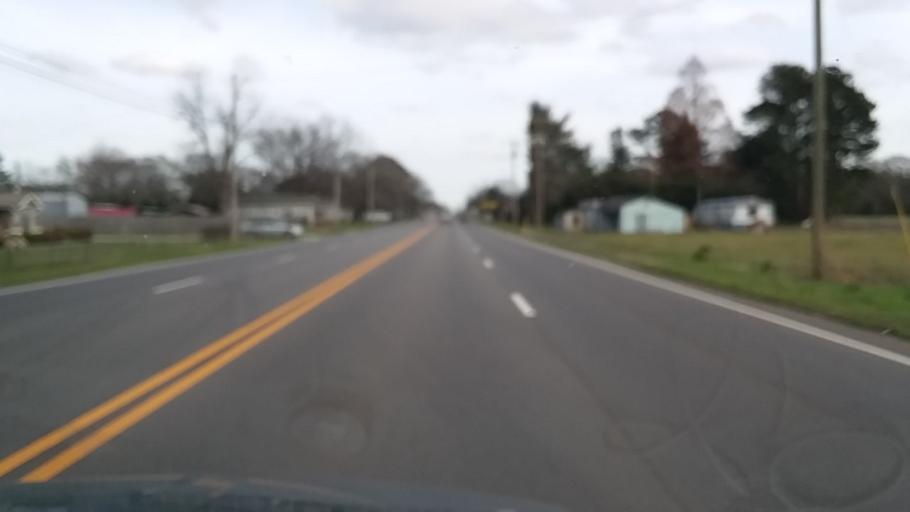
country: US
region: Alabama
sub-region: Lawrence County
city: Town Creek
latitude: 34.6813
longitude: -87.4136
